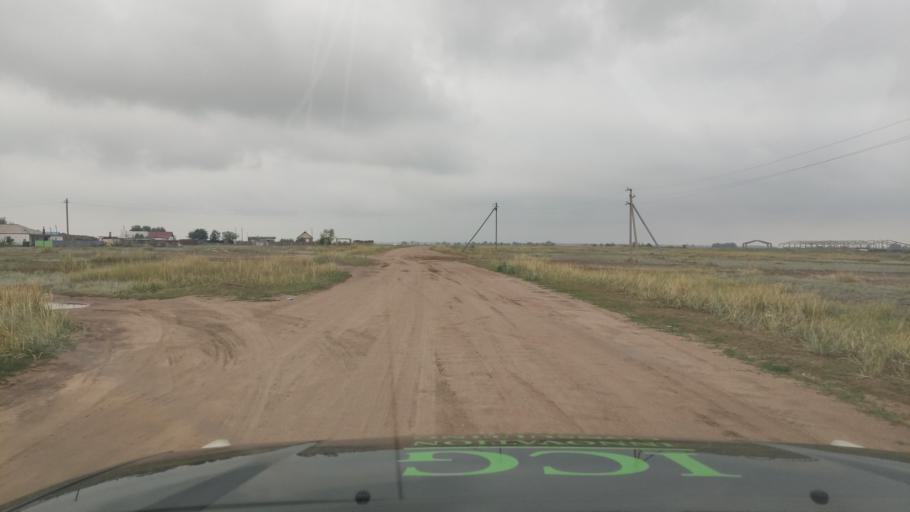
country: KZ
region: Pavlodar
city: Aksu
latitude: 52.0851
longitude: 77.1194
